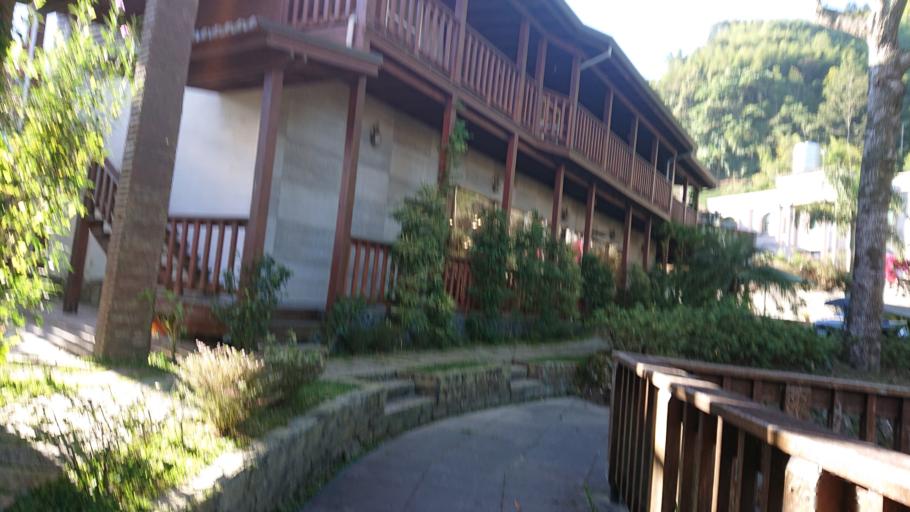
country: TW
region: Taiwan
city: Lugu
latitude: 23.5440
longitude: 120.6879
